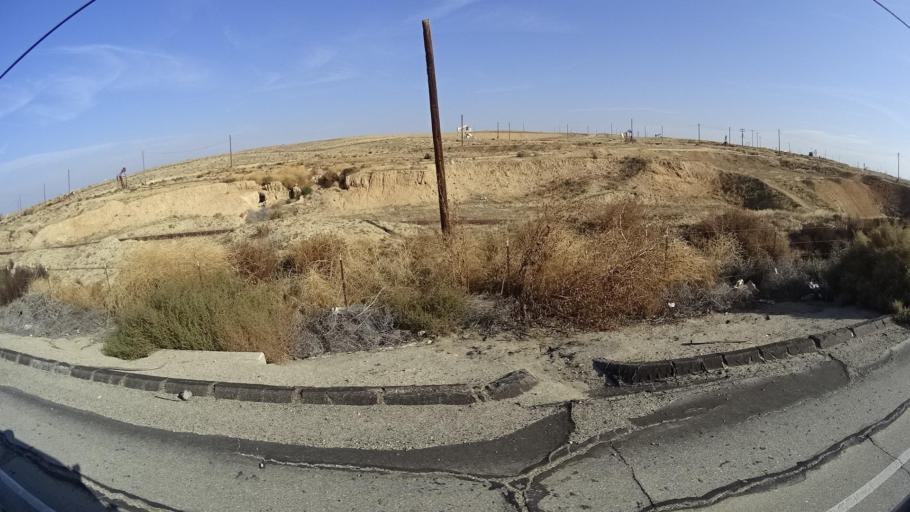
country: US
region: California
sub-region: Kern County
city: Oildale
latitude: 35.4692
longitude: -119.0641
